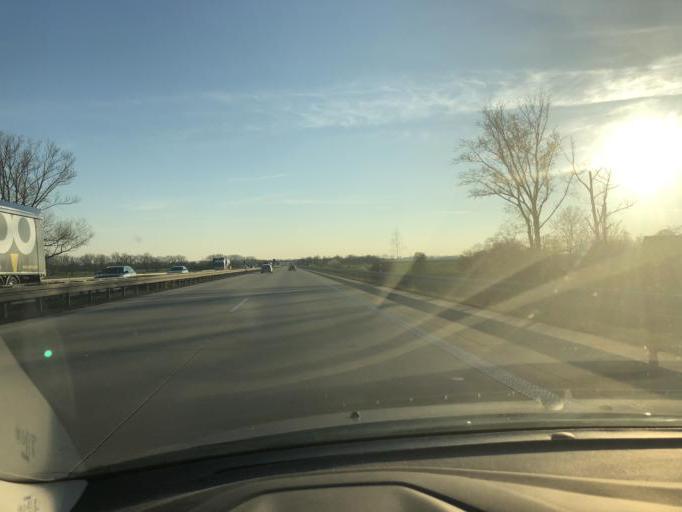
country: DE
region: Saxony
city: Kitzen
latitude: 51.2478
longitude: 12.2272
